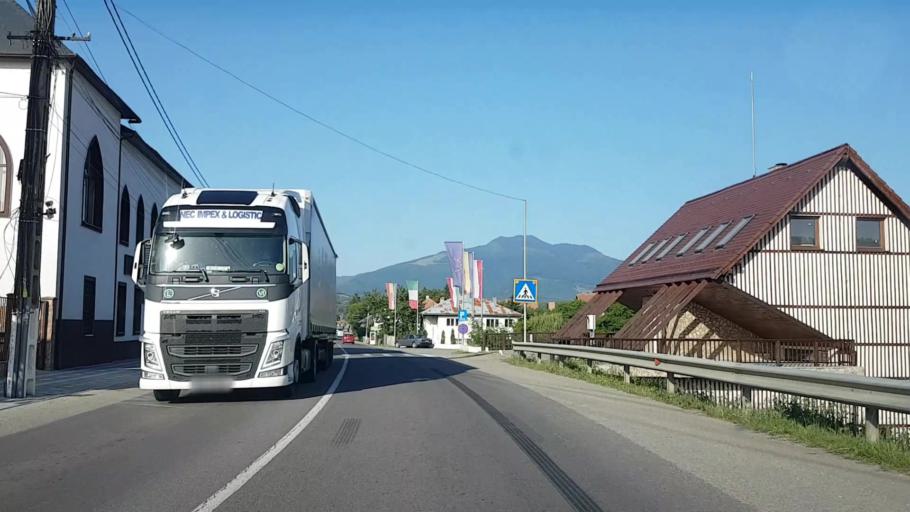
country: RO
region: Bistrita-Nasaud
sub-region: Comuna Bistrita Bargaului
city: Bistrita Bargaului
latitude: 47.2200
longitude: 24.7433
